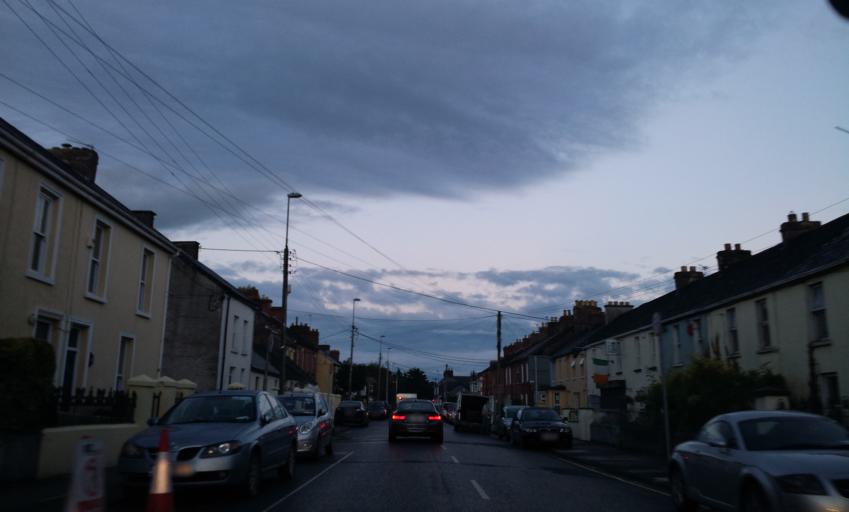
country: IE
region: Munster
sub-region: County Limerick
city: Luimneach
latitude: 52.6511
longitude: -8.6393
